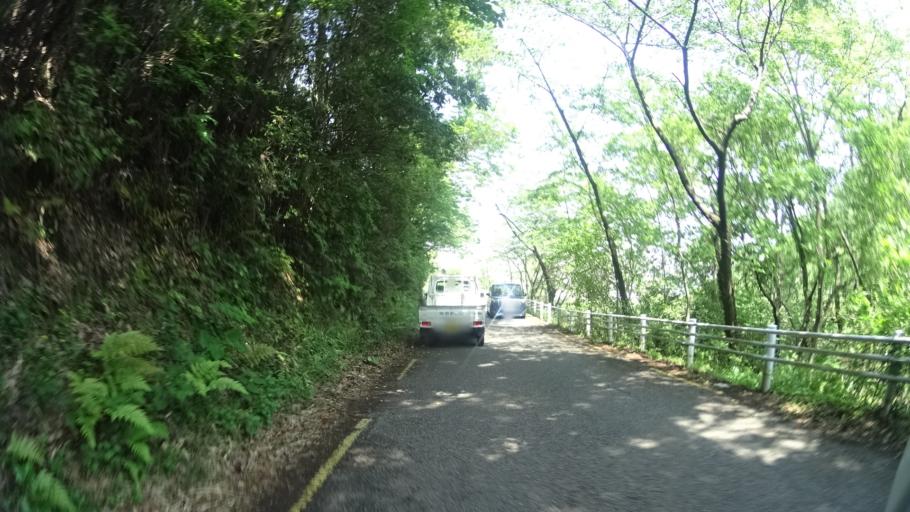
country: JP
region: Tokushima
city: Tokushima-shi
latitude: 34.0690
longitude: 134.5129
